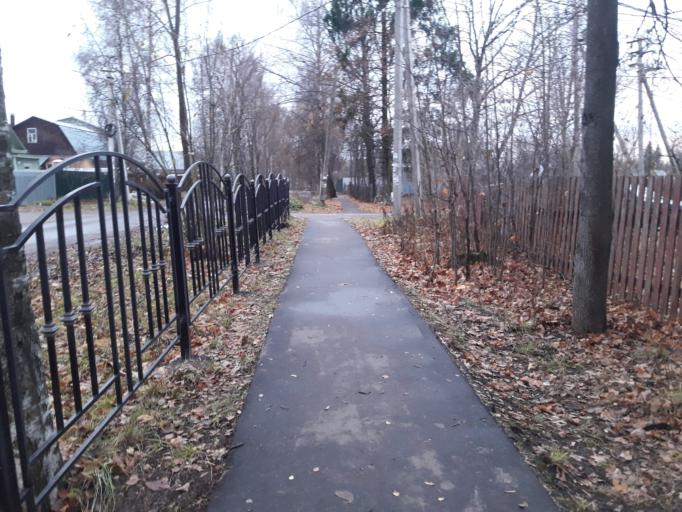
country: RU
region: Moskovskaya
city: Ashukino
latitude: 56.1691
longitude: 37.9433
